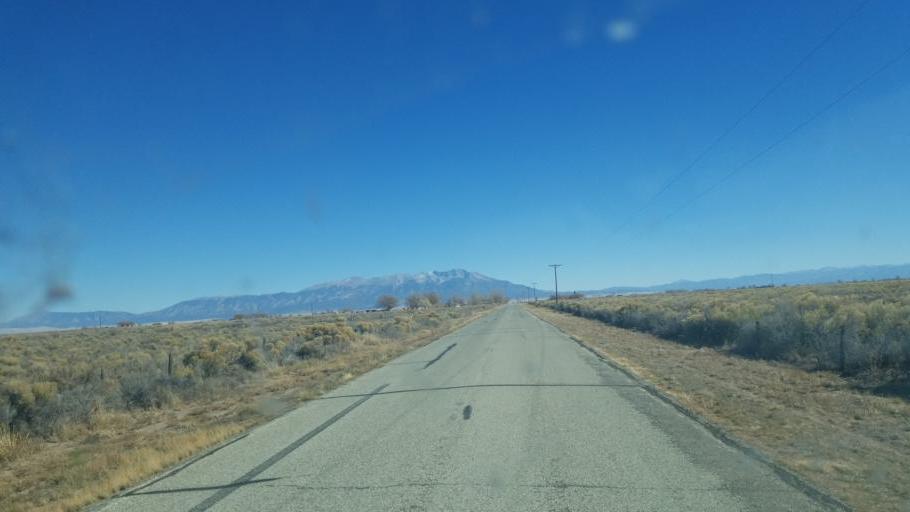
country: US
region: Colorado
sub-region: Alamosa County
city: Alamosa
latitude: 37.5306
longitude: -105.9169
